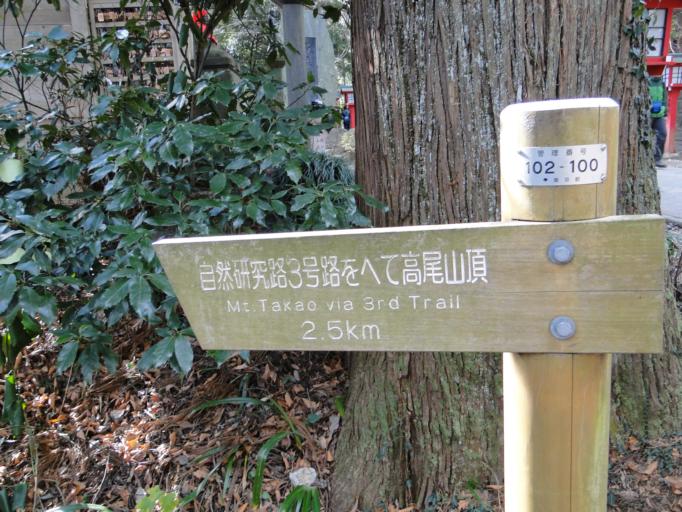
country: JP
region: Tokyo
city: Hachioji
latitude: 35.6298
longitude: 139.2532
